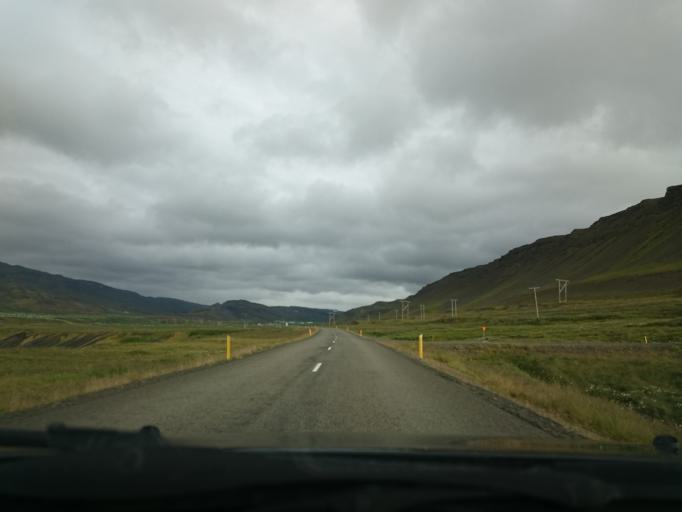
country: IS
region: West
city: Stykkisholmur
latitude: 65.4589
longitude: -21.9166
